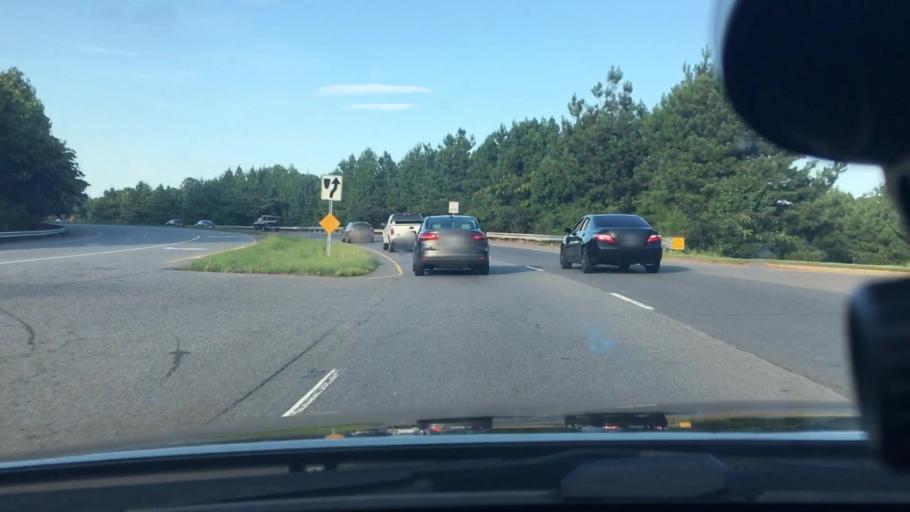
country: US
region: North Carolina
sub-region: Mecklenburg County
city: Mint Hill
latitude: 35.2092
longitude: -80.6640
